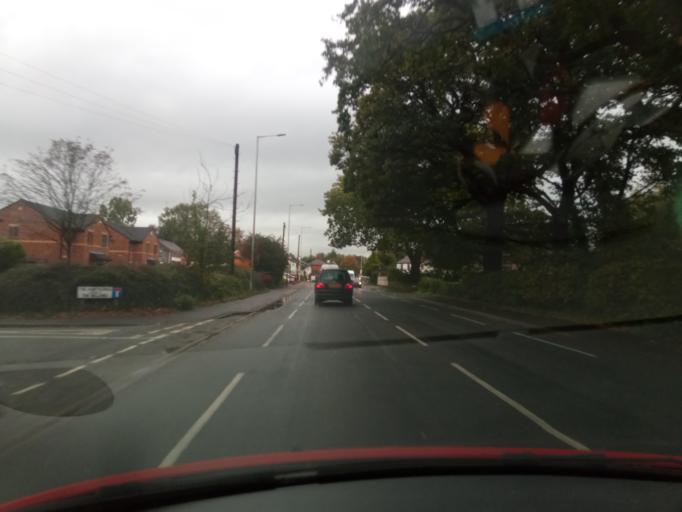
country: GB
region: England
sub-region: Lancashire
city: Catterall
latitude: 53.8560
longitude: -2.7449
